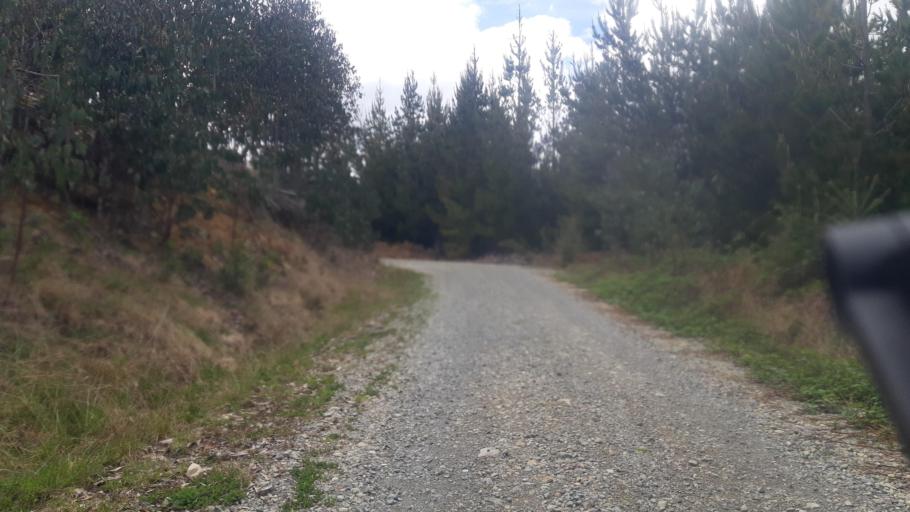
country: NZ
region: Tasman
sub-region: Tasman District
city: Wakefield
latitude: -41.7693
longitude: 172.7998
